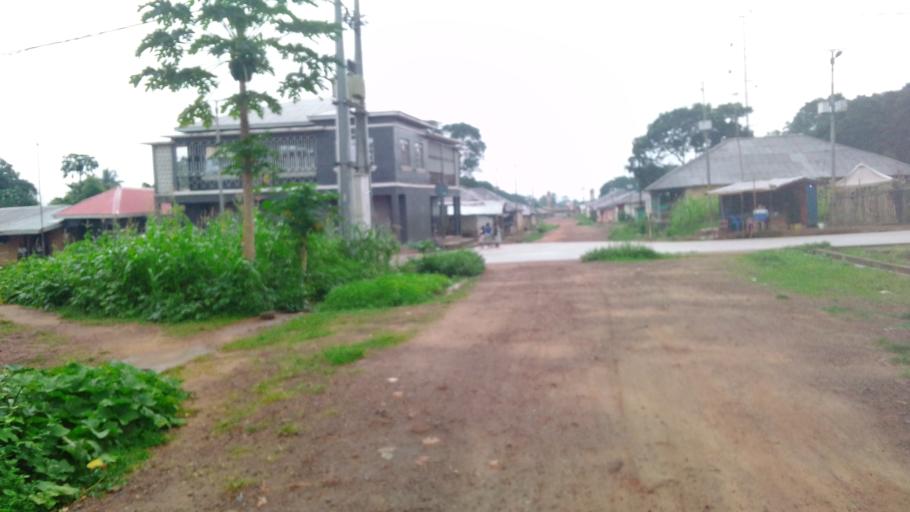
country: SL
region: Northern Province
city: Lunsar
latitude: 8.6843
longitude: -12.5307
